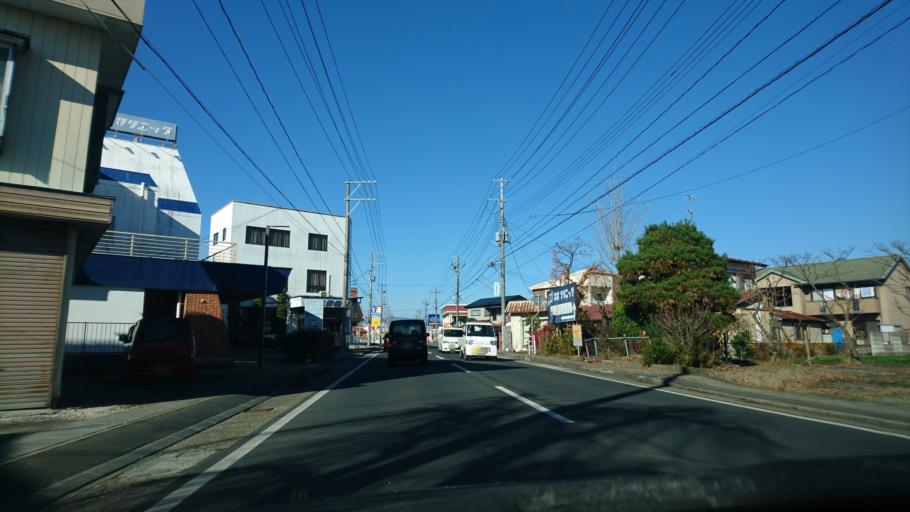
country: JP
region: Iwate
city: Mizusawa
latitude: 39.1398
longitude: 141.1327
